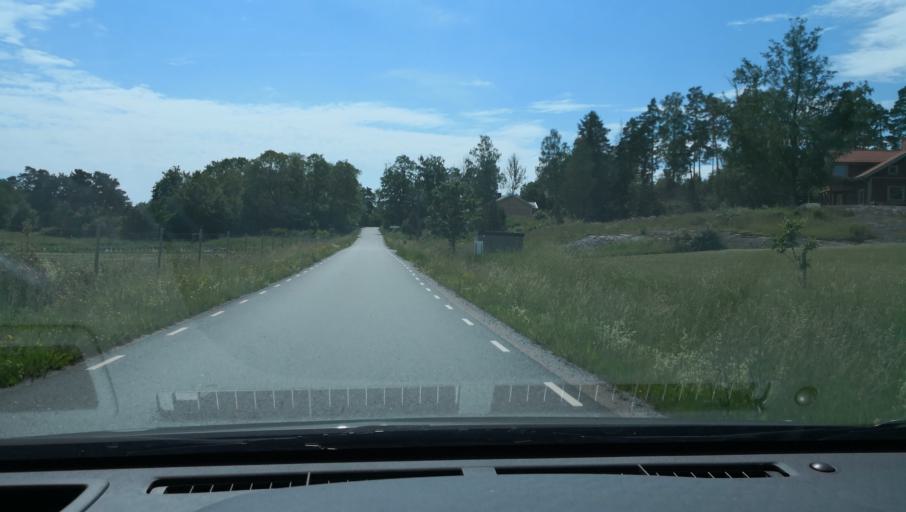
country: SE
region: Uppsala
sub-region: Habo Kommun
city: Balsta
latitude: 59.6732
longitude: 17.4637
